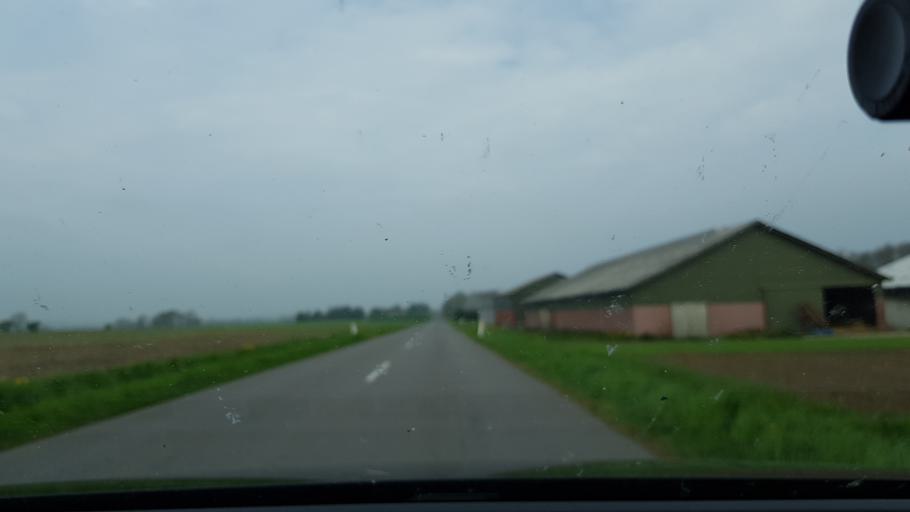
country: DK
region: Capital Region
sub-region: Bornholm Kommune
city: Nexo
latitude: 55.0140
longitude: 15.0961
